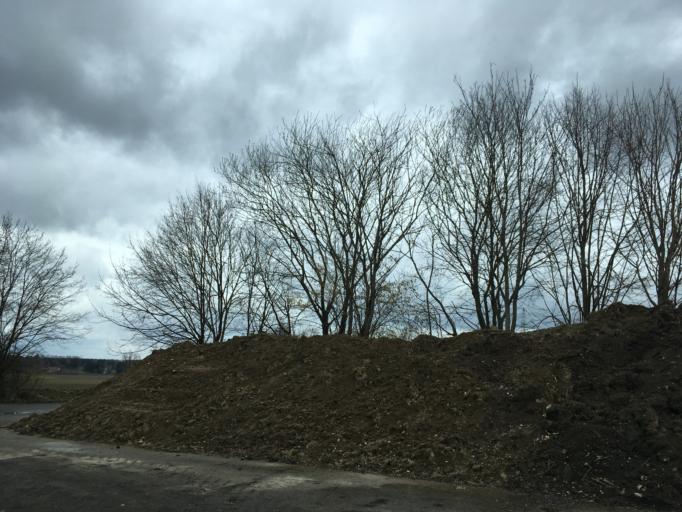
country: DE
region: Bavaria
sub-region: Upper Bavaria
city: Markt Schwaben
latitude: 48.1742
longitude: 11.8607
